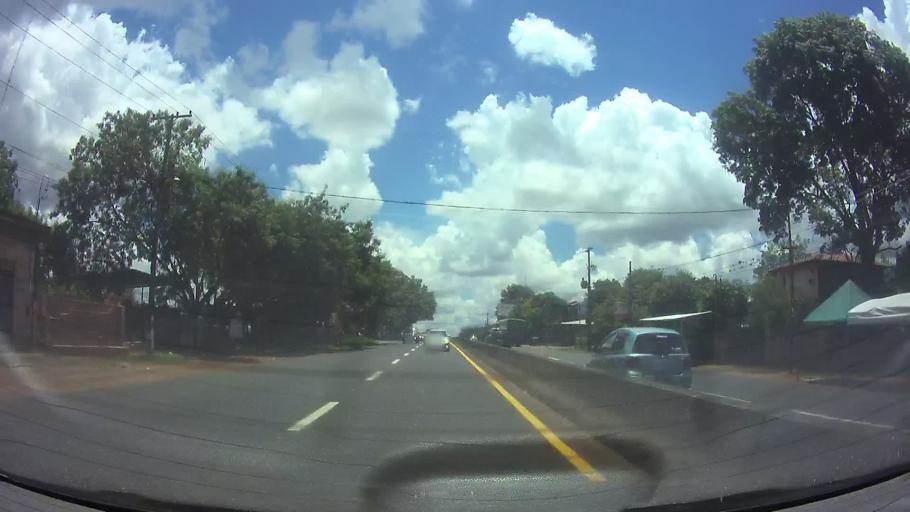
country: PY
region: Central
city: Itaugua
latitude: -25.3787
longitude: -57.3875
